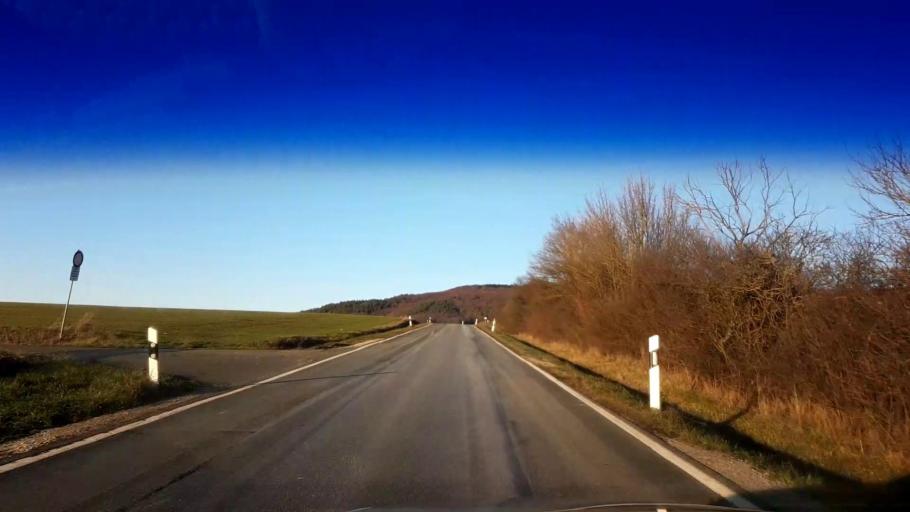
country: DE
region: Bavaria
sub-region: Upper Franconia
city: Buttenheim
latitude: 49.8294
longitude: 11.0293
